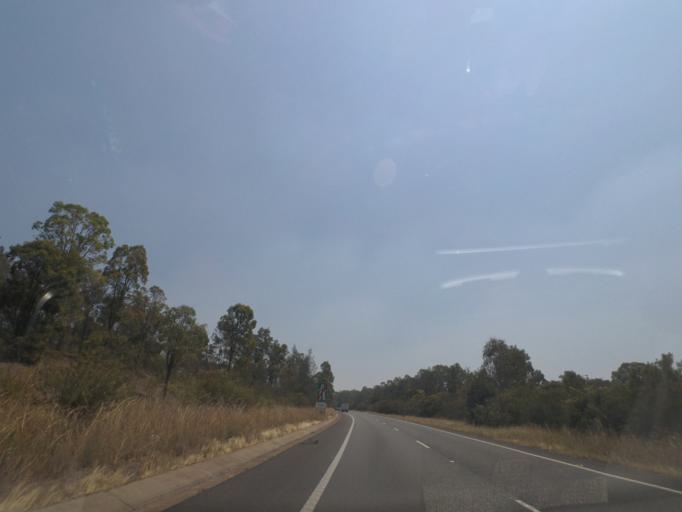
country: AU
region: New South Wales
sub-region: Newcastle
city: Beresfield
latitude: -32.8369
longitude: 151.6349
